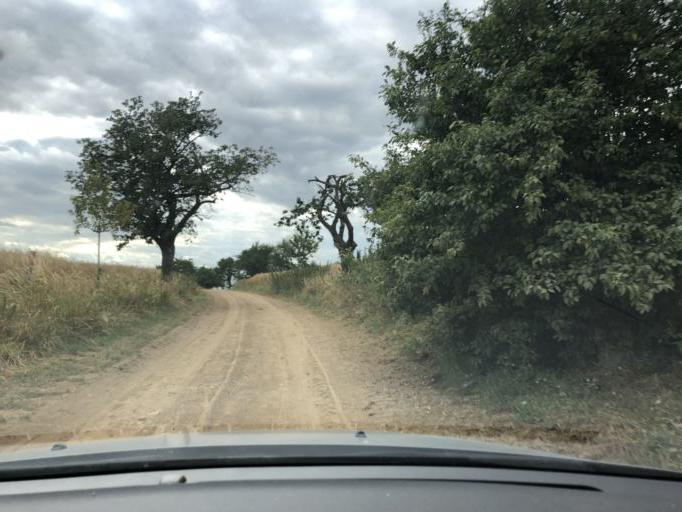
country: DE
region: Saxony
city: Geithain
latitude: 51.0266
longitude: 12.6298
